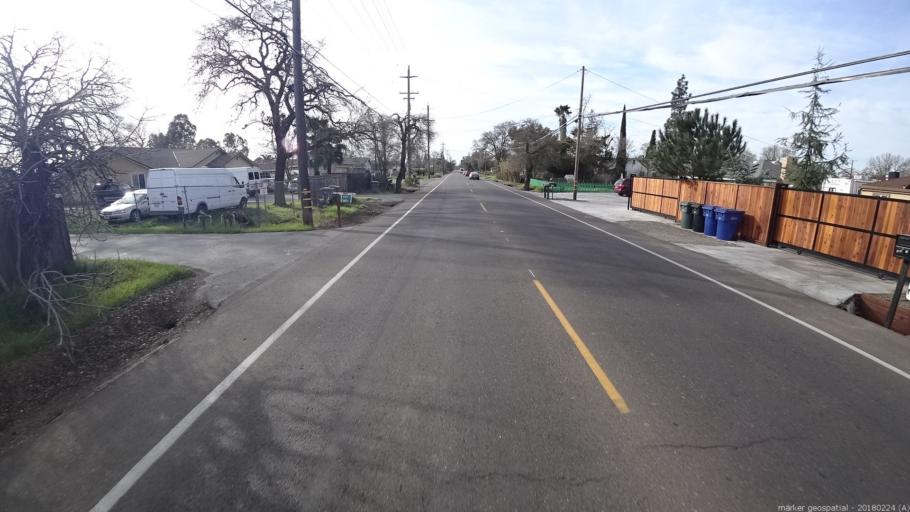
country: US
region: California
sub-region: Sacramento County
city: Rio Linda
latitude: 38.6810
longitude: -121.4569
